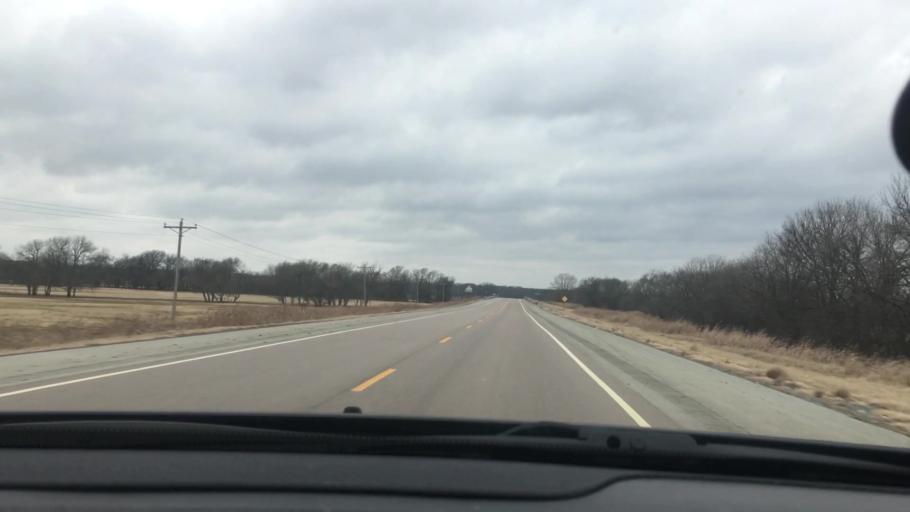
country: US
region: Oklahoma
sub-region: Atoka County
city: Atoka
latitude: 34.3709
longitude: -96.3165
